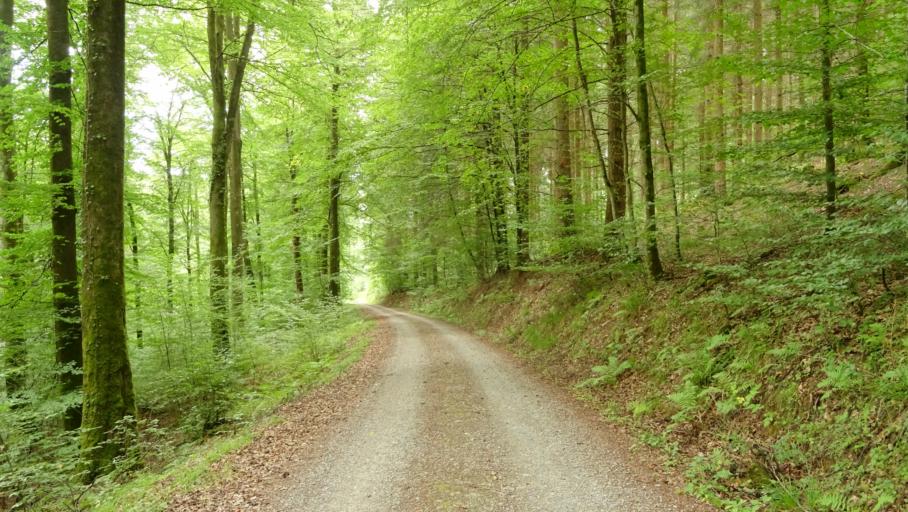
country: DE
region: Baden-Wuerttemberg
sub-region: Karlsruhe Region
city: Fahrenbach
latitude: 49.4256
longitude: 9.1173
